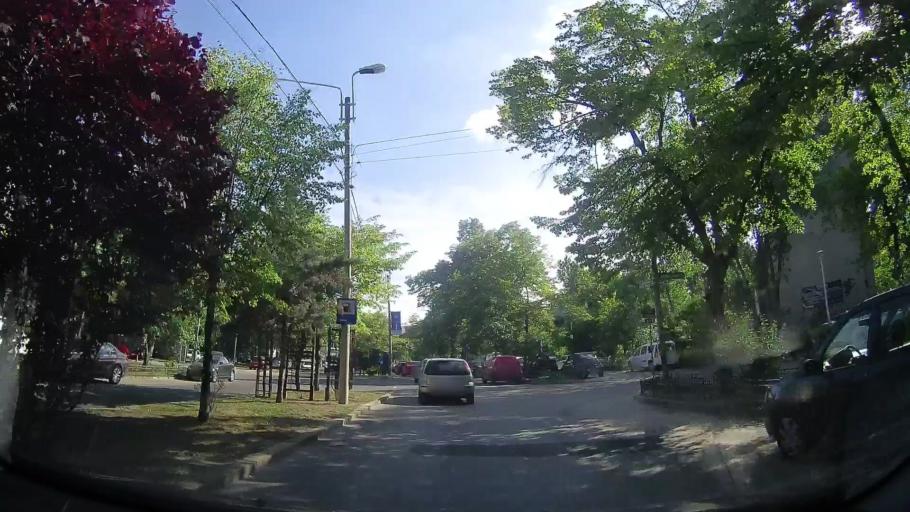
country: RO
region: Ilfov
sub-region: Comuna Chiajna
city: Rosu
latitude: 44.4262
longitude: 26.0474
